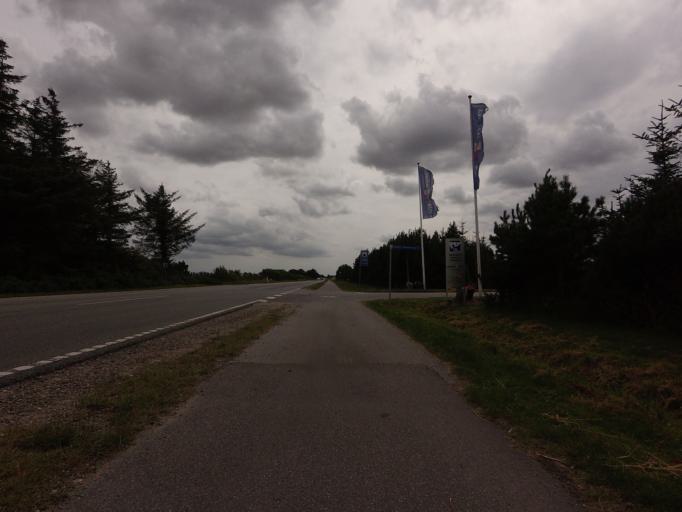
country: DK
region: North Denmark
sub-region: Jammerbugt Kommune
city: Pandrup
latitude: 57.3444
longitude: 9.7077
